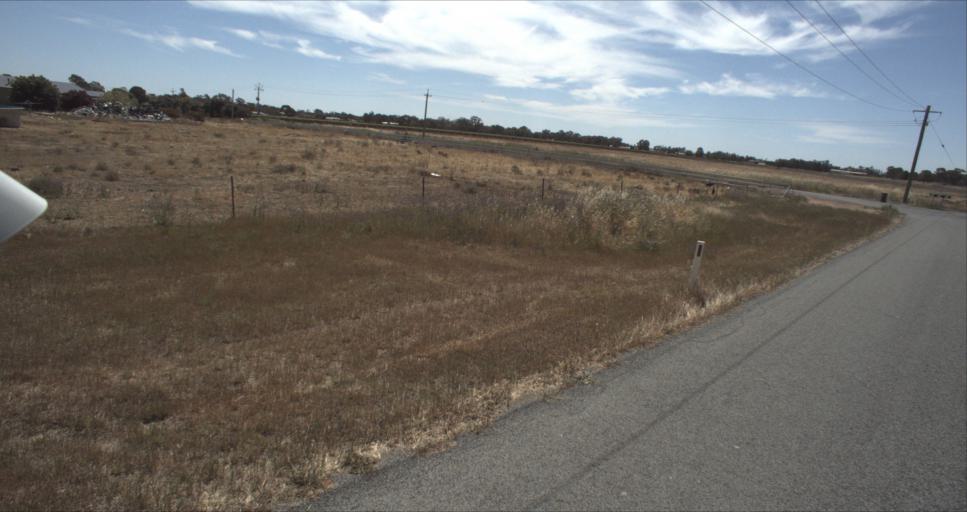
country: AU
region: New South Wales
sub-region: Leeton
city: Leeton
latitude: -34.5733
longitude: 146.4219
